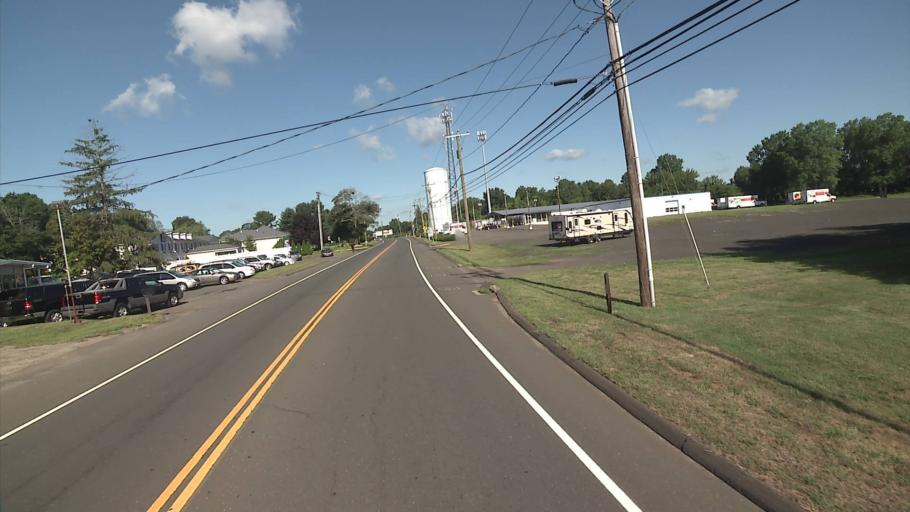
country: US
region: Connecticut
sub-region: New Haven County
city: Guilford Center
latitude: 41.2875
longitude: -72.6563
